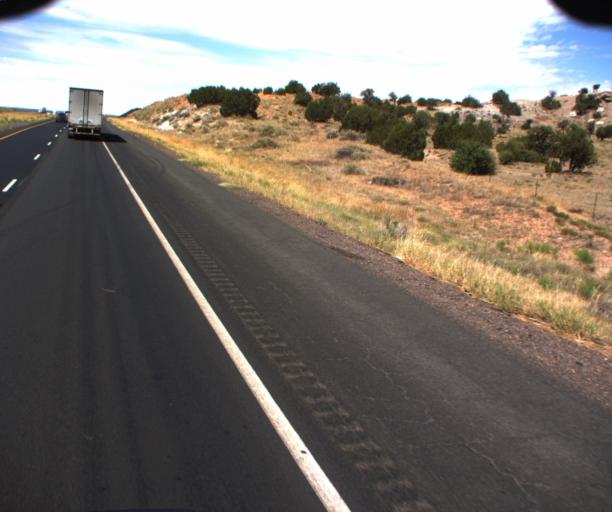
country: US
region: Arizona
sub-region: Apache County
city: Houck
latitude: 35.3187
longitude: -109.0914
